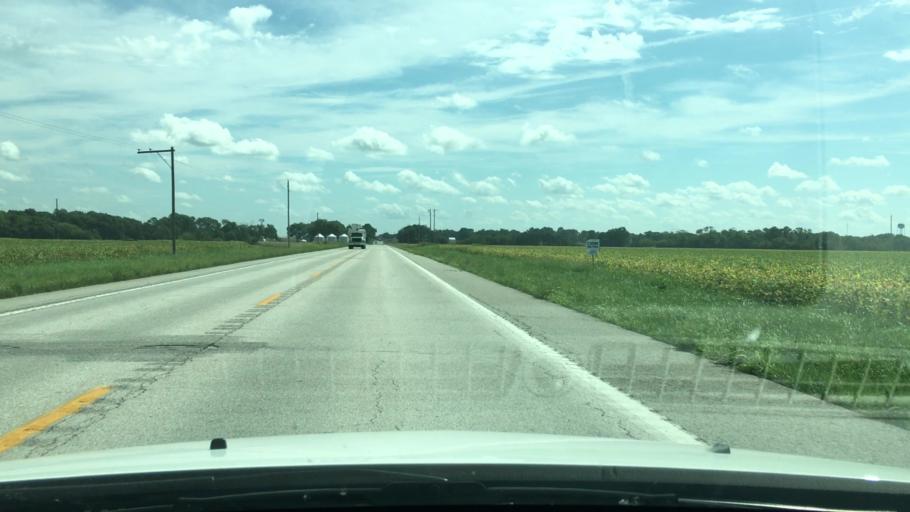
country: US
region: Missouri
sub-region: Audrain County
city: Vandalia
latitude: 39.2797
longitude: -91.5929
